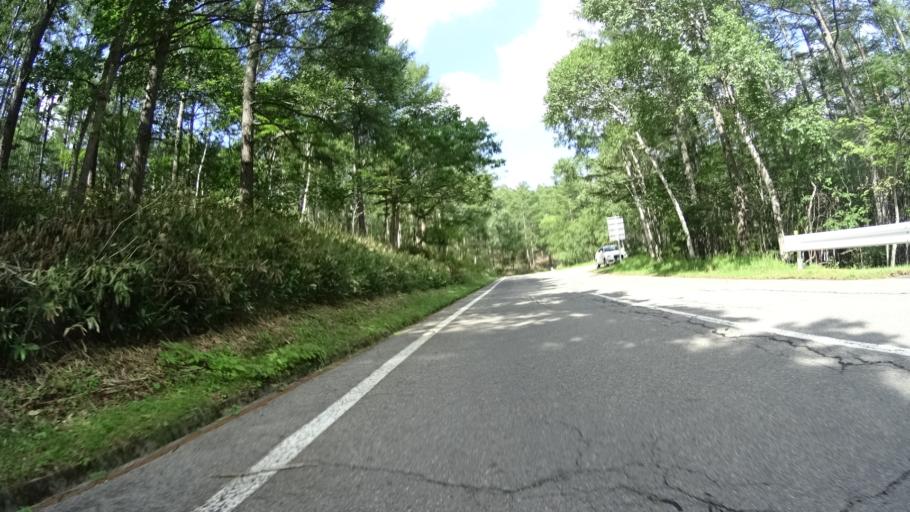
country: JP
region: Nagano
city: Saku
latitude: 36.0612
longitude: 138.3921
